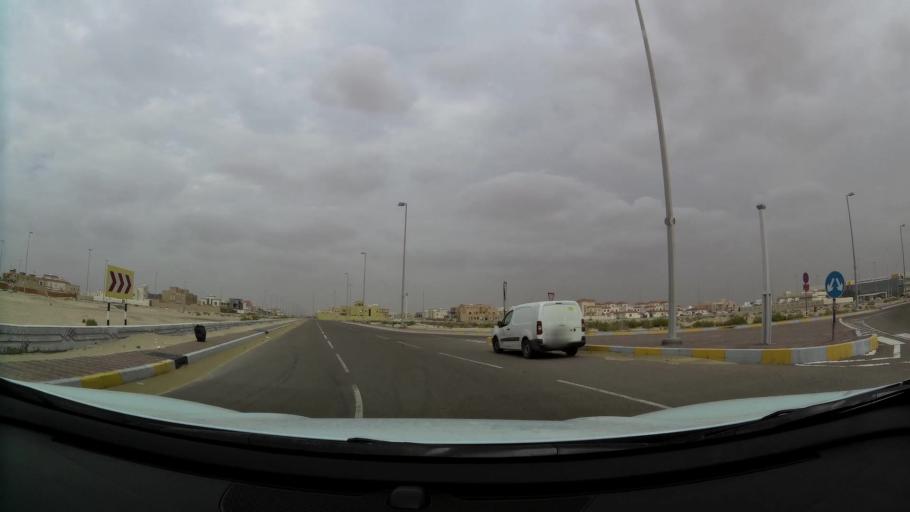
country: AE
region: Abu Dhabi
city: Abu Dhabi
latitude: 24.3920
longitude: 54.6507
